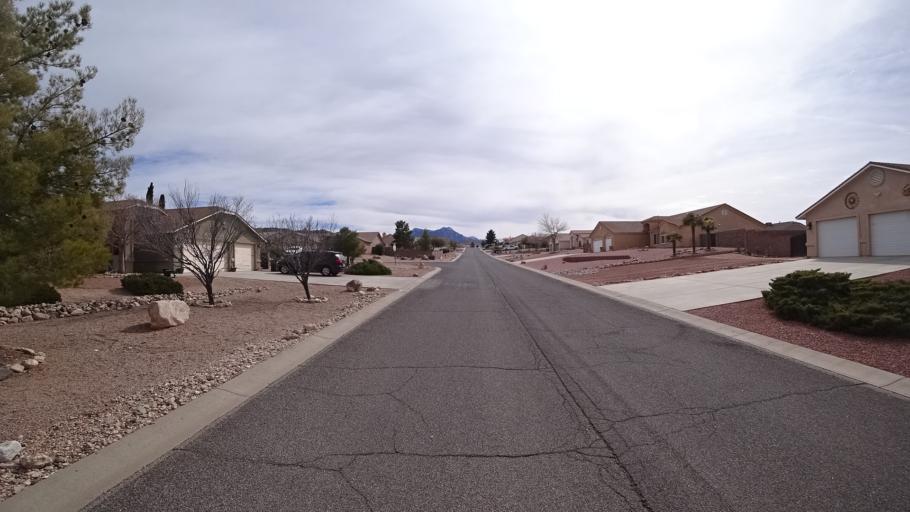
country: US
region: Arizona
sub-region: Mohave County
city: Kingman
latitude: 35.1931
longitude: -113.9811
